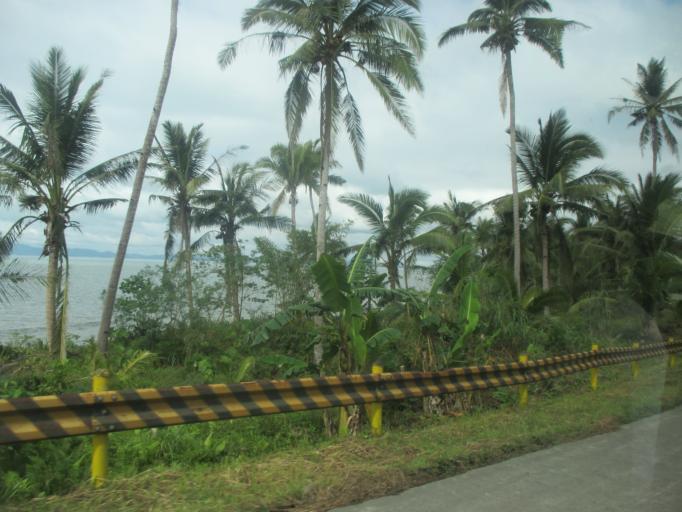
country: PH
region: Eastern Visayas
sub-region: Province of Samar
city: Basey
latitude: 11.2450
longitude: 125.1729
